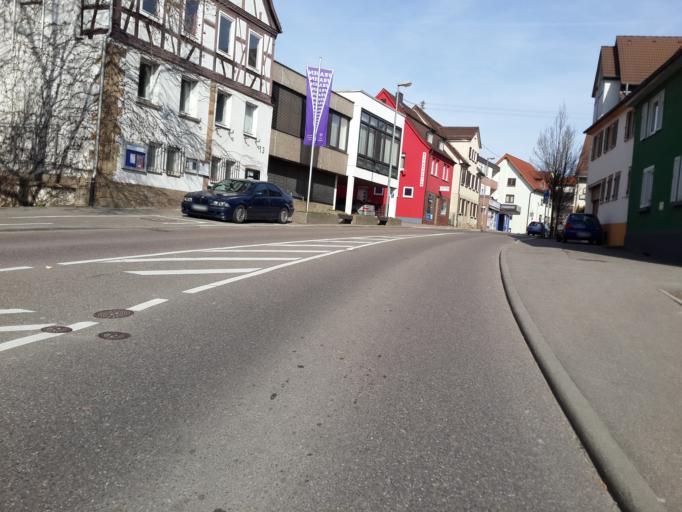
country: DE
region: Baden-Wuerttemberg
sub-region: Regierungsbezirk Stuttgart
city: Heilbronn
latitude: 49.1590
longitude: 9.1722
